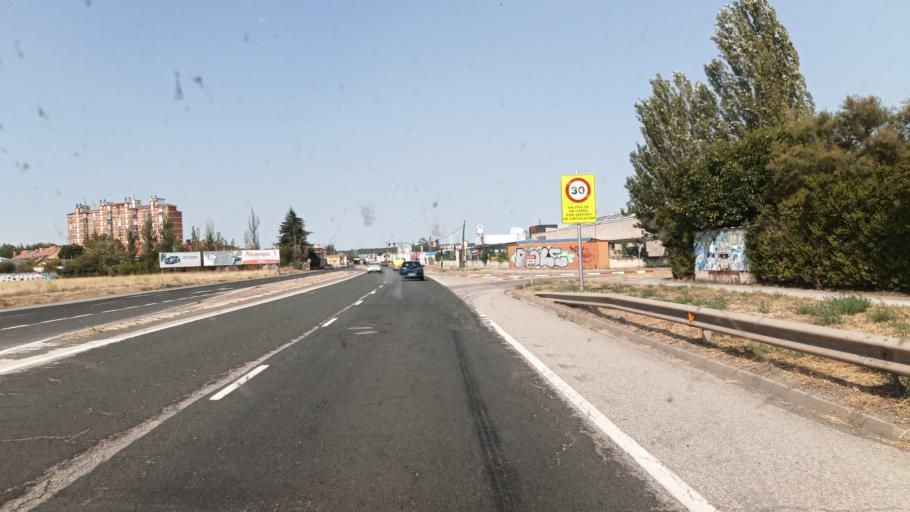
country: ES
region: Castille and Leon
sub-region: Provincia de Burgos
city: Cardenajimeno
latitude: 42.3447
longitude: -3.6444
